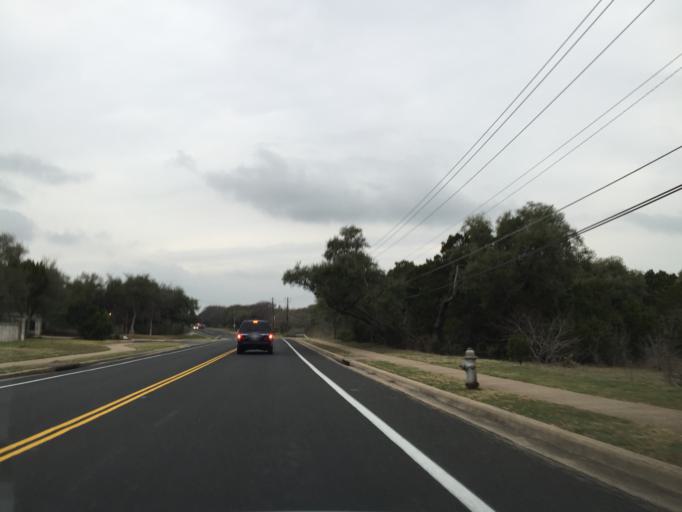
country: US
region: Texas
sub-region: Travis County
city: Lost Creek
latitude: 30.2440
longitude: -97.8356
